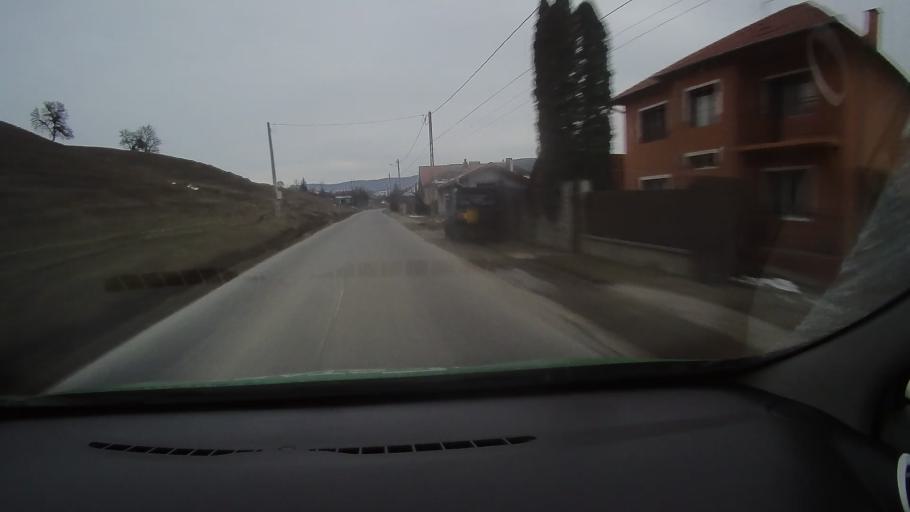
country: RO
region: Harghita
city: Taureni
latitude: 46.2555
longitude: 25.2532
